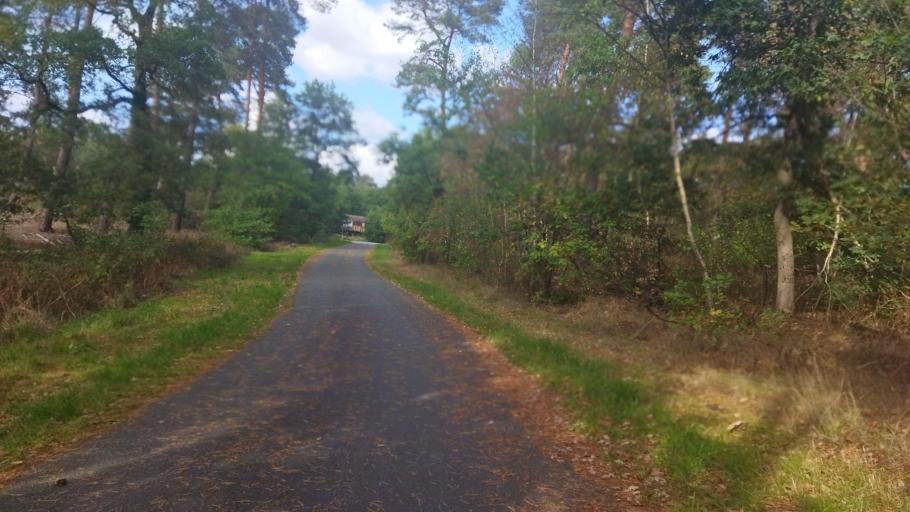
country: DE
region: North Rhine-Westphalia
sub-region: Regierungsbezirk Munster
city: Dulmen
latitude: 51.7970
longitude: 7.2579
